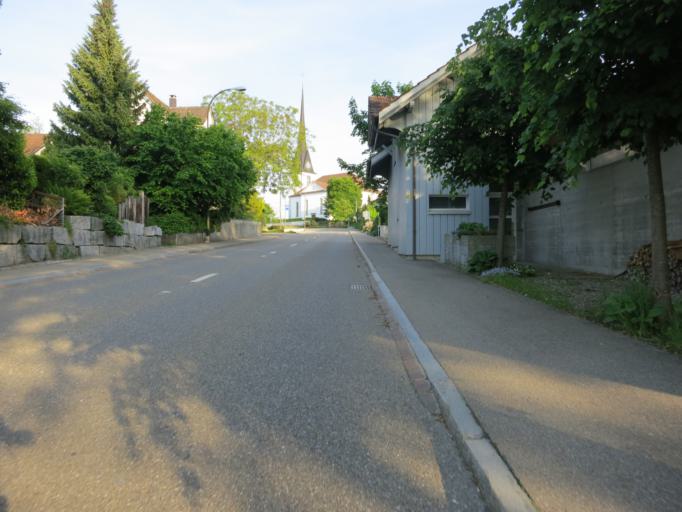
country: CH
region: Zurich
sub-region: Bezirk Hinwil
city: Gossau
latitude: 47.3023
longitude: 8.7608
